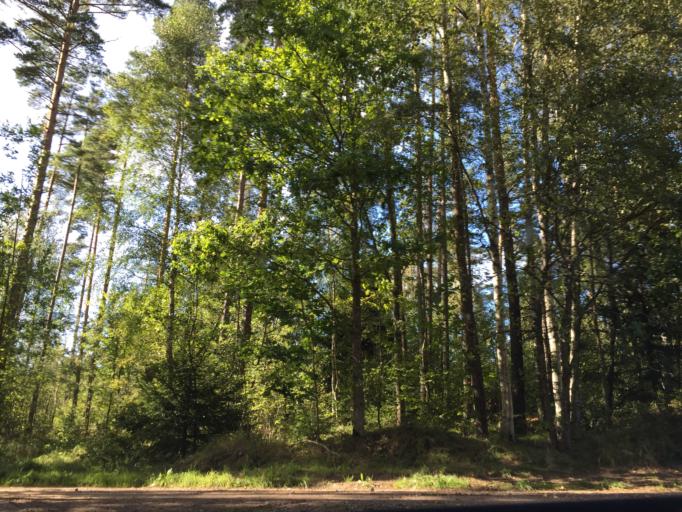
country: LV
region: Kuldigas Rajons
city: Kuldiga
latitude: 56.9926
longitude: 21.8070
